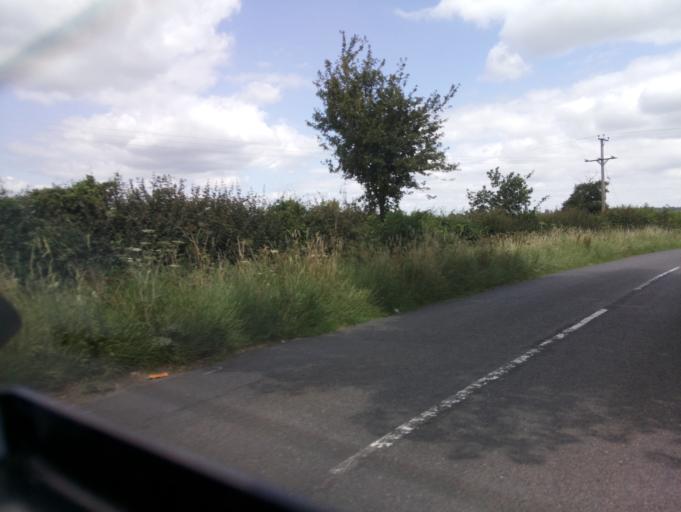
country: GB
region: England
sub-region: Buckinghamshire
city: Winslow
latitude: 51.9210
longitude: -0.8396
